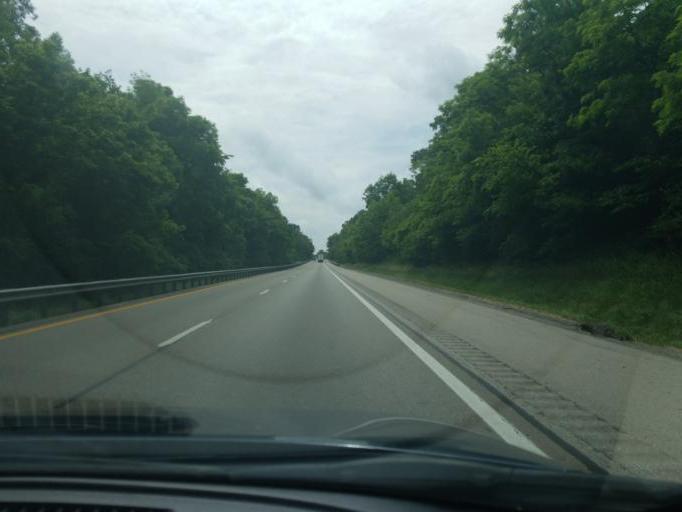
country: US
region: Indiana
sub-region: Switzerland County
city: Vevay
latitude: 38.6766
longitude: -84.9942
